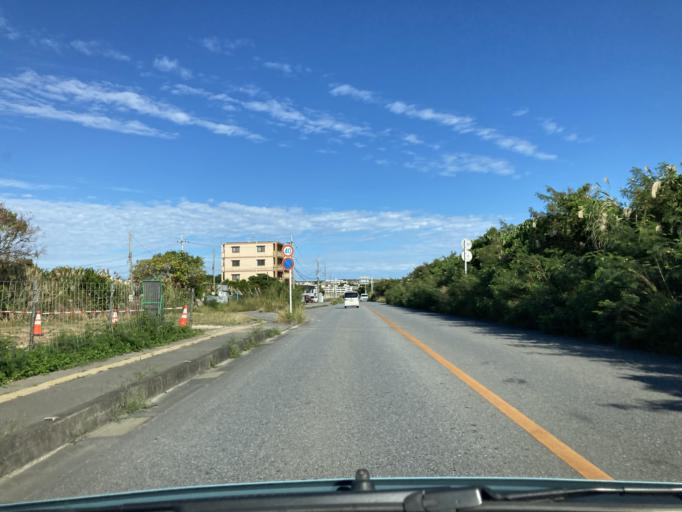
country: JP
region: Okinawa
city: Okinawa
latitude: 26.3720
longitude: 127.7462
